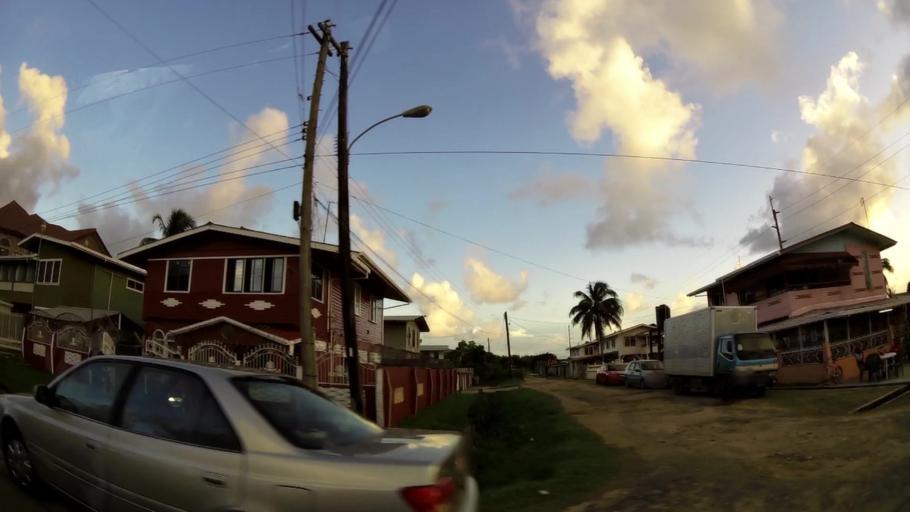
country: GY
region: Demerara-Mahaica
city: Georgetown
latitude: 6.8148
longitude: -58.1037
